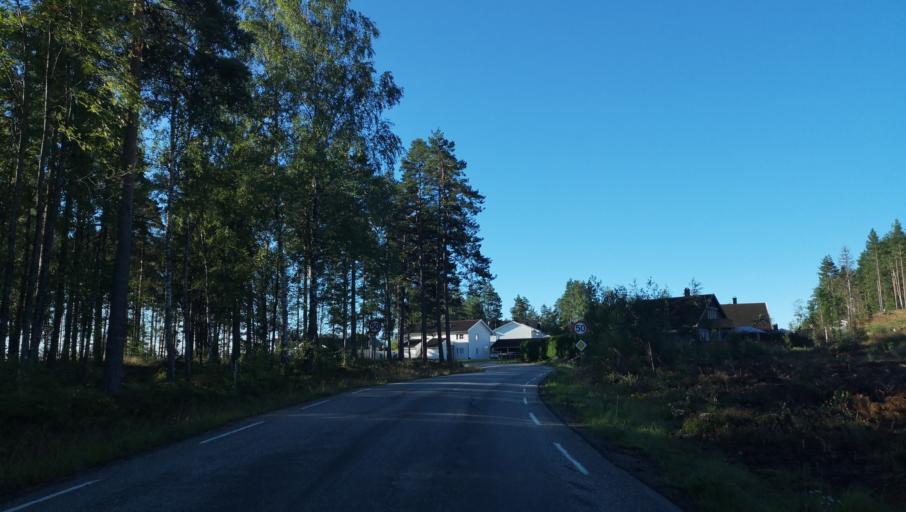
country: NO
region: Ostfold
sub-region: Hobol
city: Knappstad
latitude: 59.6325
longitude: 11.0241
